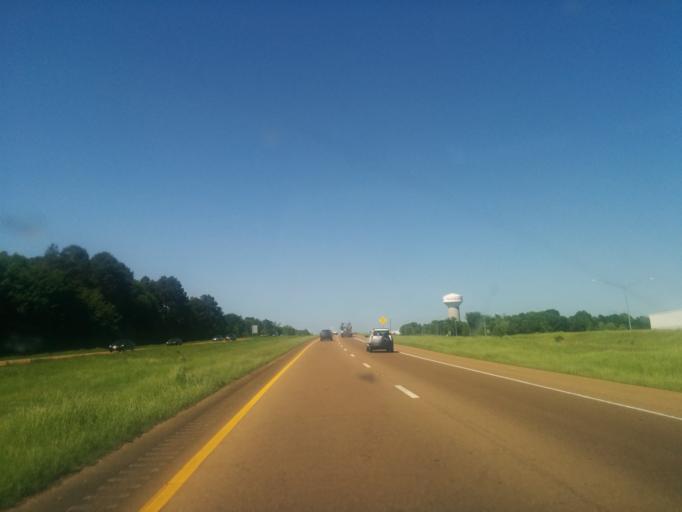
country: US
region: Mississippi
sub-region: Madison County
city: Canton
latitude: 32.5579
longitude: -90.0834
